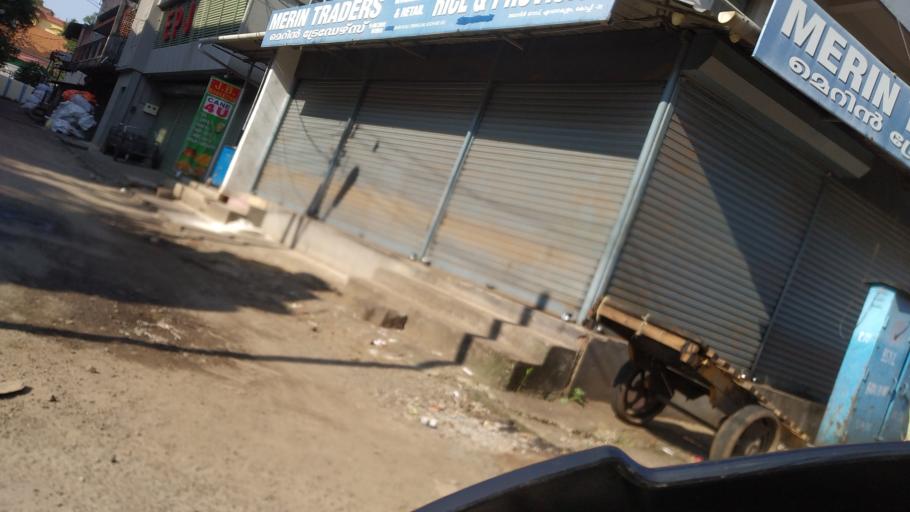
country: IN
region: Kerala
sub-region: Ernakulam
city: Cochin
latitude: 9.9819
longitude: 76.2788
